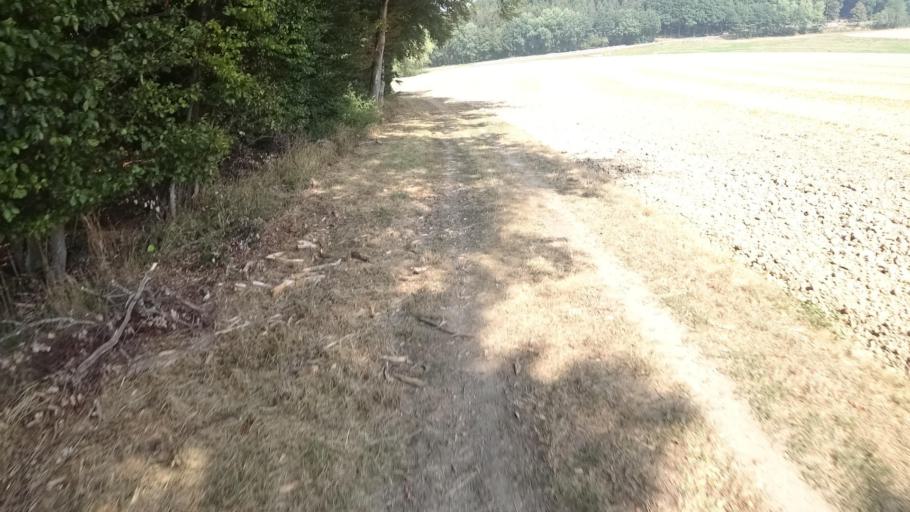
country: DE
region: Rheinland-Pfalz
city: Wahlbach
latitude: 49.9936
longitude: 7.5922
